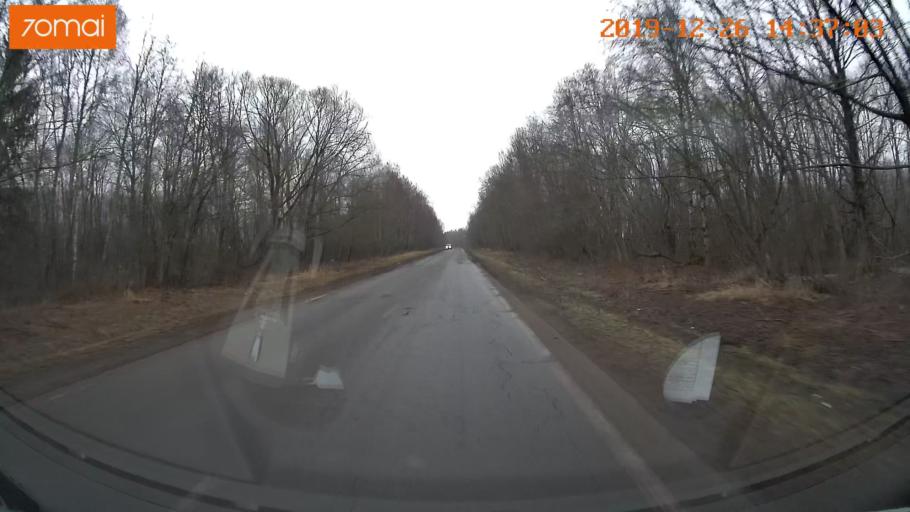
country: RU
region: Jaroslavl
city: Poshekhon'ye
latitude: 58.4058
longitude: 38.9738
